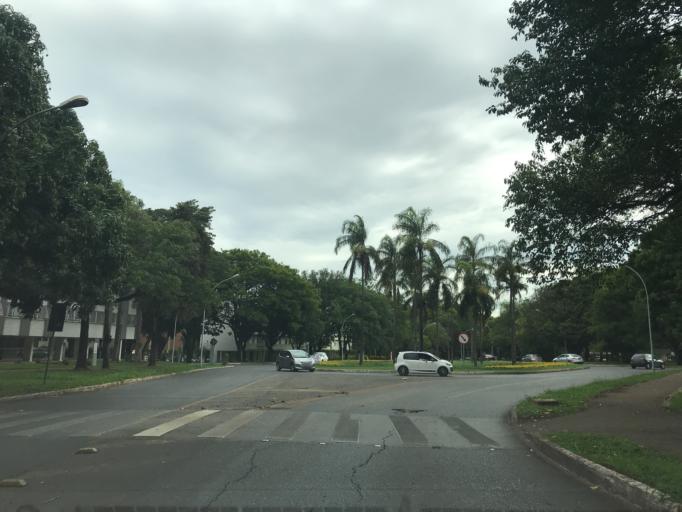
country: BR
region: Federal District
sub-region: Brasilia
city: Brasilia
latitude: -15.8101
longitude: -47.8882
